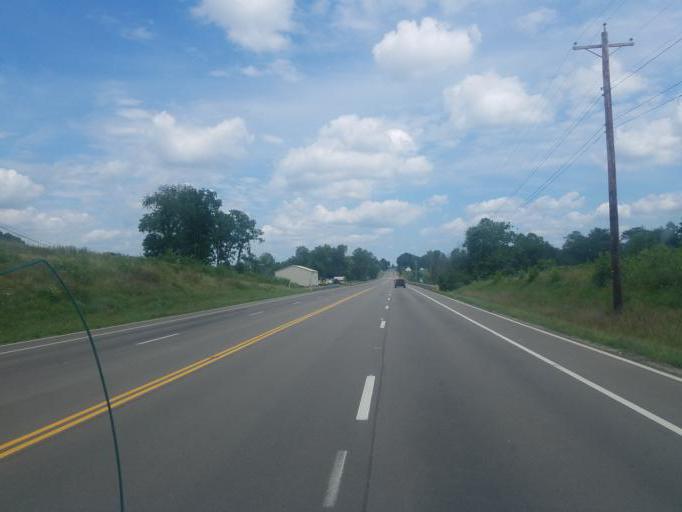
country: US
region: Ohio
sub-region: Perry County
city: Somerset
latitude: 39.9474
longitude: -82.2334
